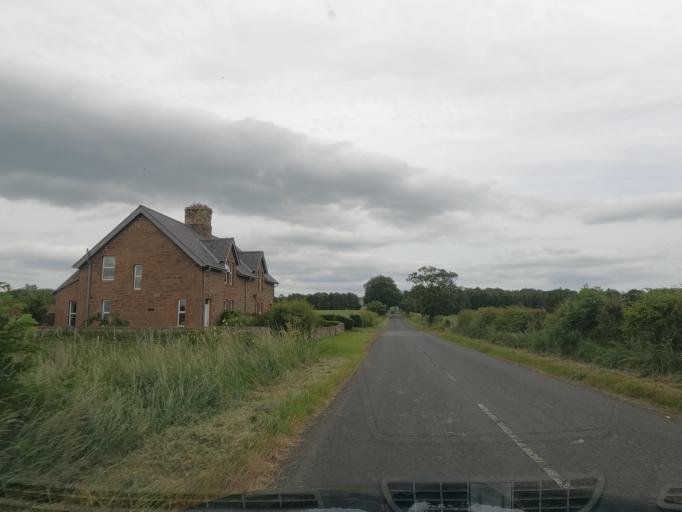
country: GB
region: England
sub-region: Northumberland
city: Doddington
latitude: 55.5622
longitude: -1.9300
